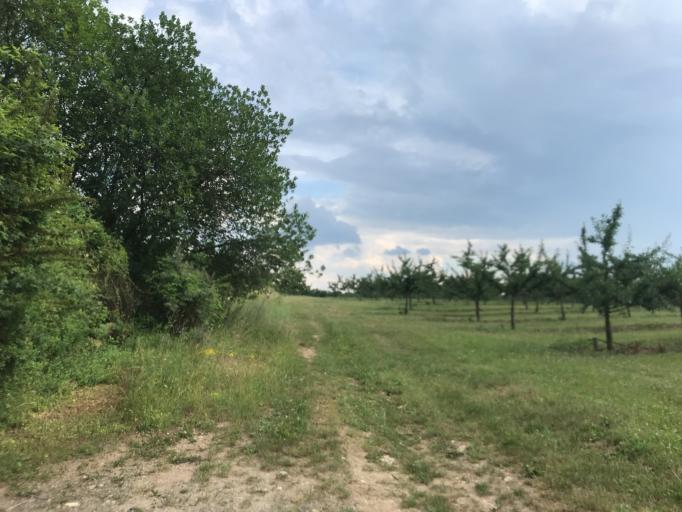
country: DE
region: Rheinland-Pfalz
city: Budenheim
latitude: 50.0034
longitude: 8.1805
